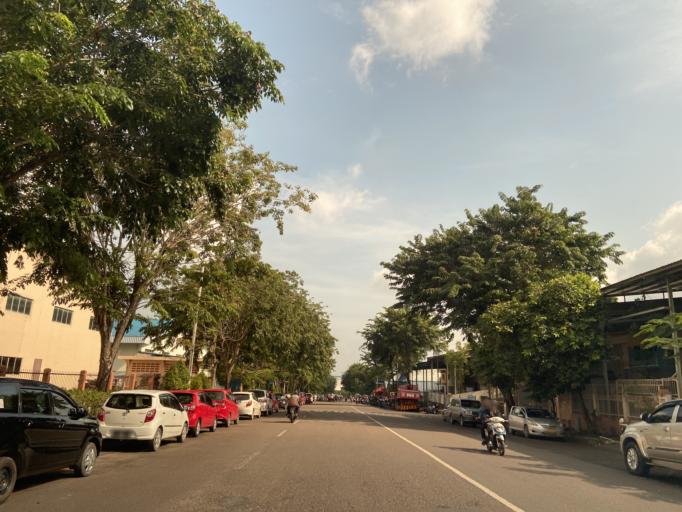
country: SG
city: Singapore
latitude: 1.1064
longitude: 104.0722
